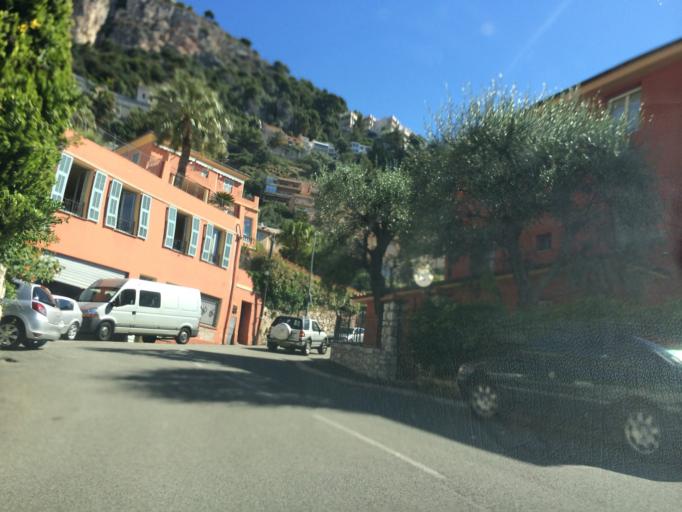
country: FR
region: Provence-Alpes-Cote d'Azur
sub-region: Departement des Alpes-Maritimes
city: Villefranche-sur-Mer
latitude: 43.7084
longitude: 7.3134
